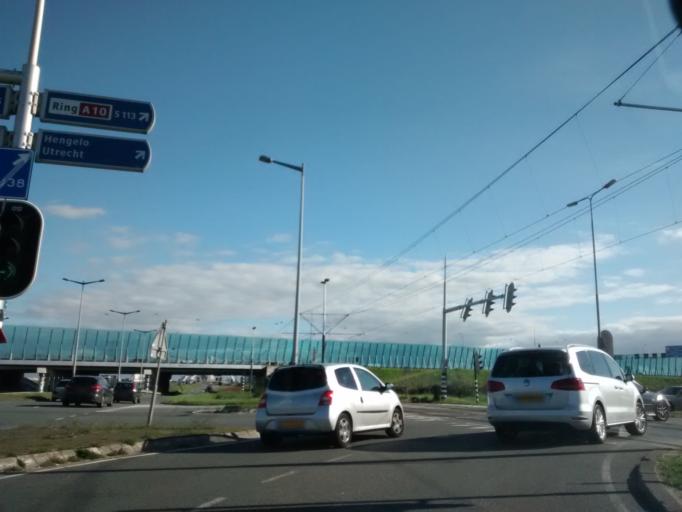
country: NL
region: North Holland
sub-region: Gemeente Diemen
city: Diemen
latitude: 52.3683
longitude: 4.9703
